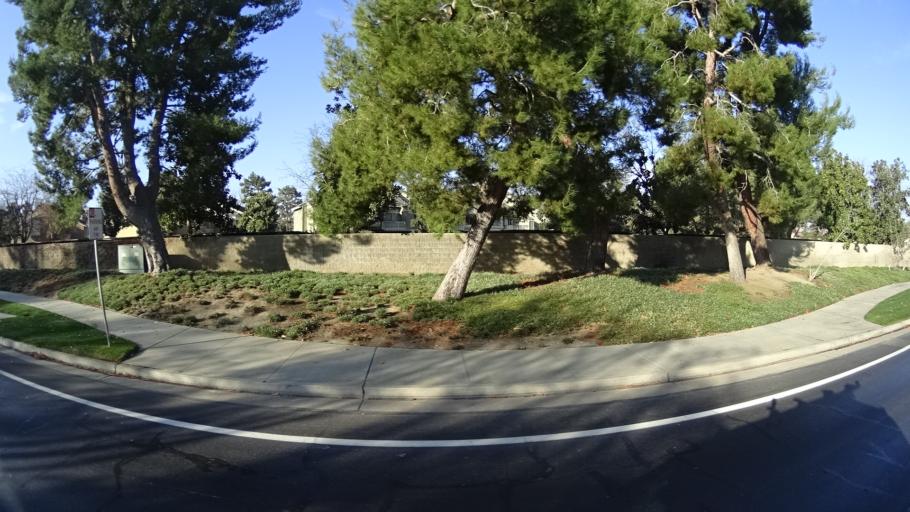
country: US
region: California
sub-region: Kern County
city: Greenacres
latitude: 35.3437
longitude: -119.0923
